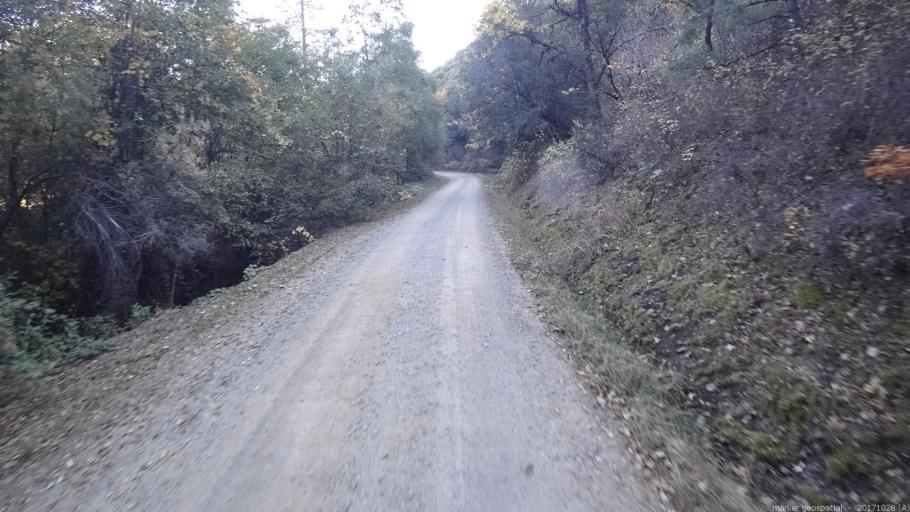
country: US
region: California
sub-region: Trinity County
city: Lewiston
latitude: 40.7152
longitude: -122.6319
